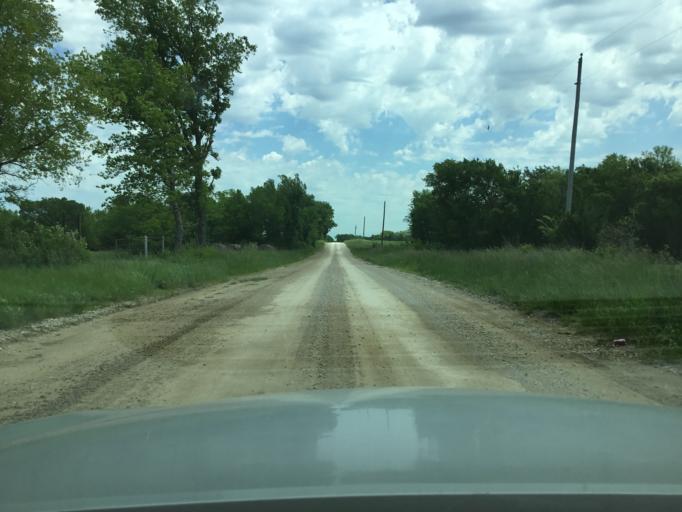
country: US
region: Kansas
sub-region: Montgomery County
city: Independence
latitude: 37.0952
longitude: -95.7888
